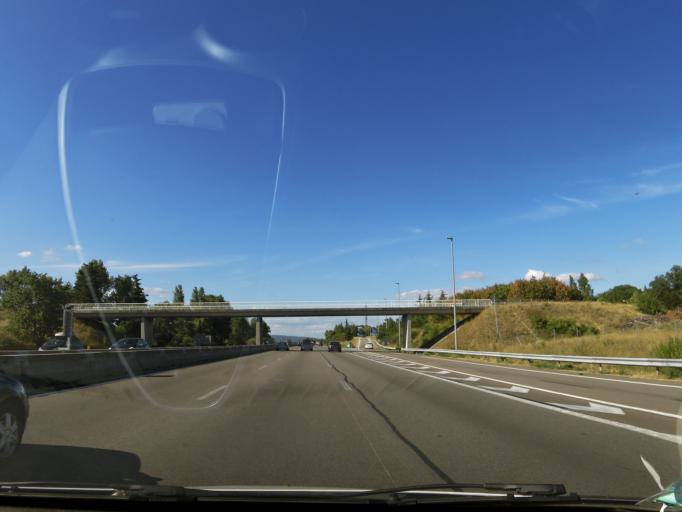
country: FR
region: Rhone-Alpes
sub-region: Departement de la Drome
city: Saulce-sur-Rhone
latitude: 44.7180
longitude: 4.7856
